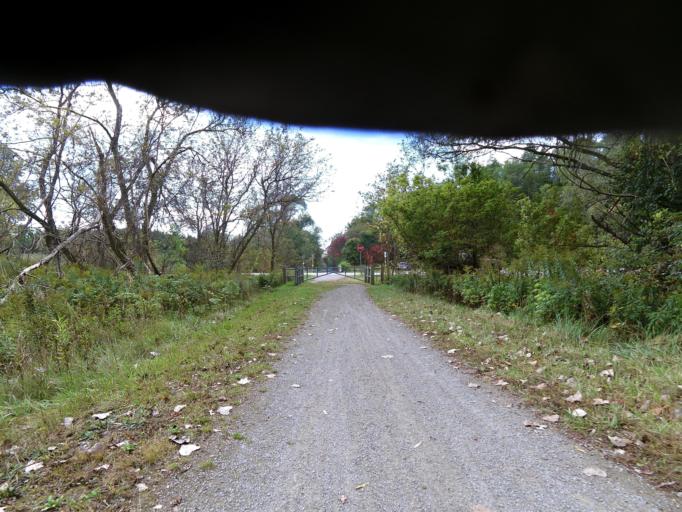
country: CA
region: Ontario
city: Ancaster
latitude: 43.2265
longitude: -80.0540
